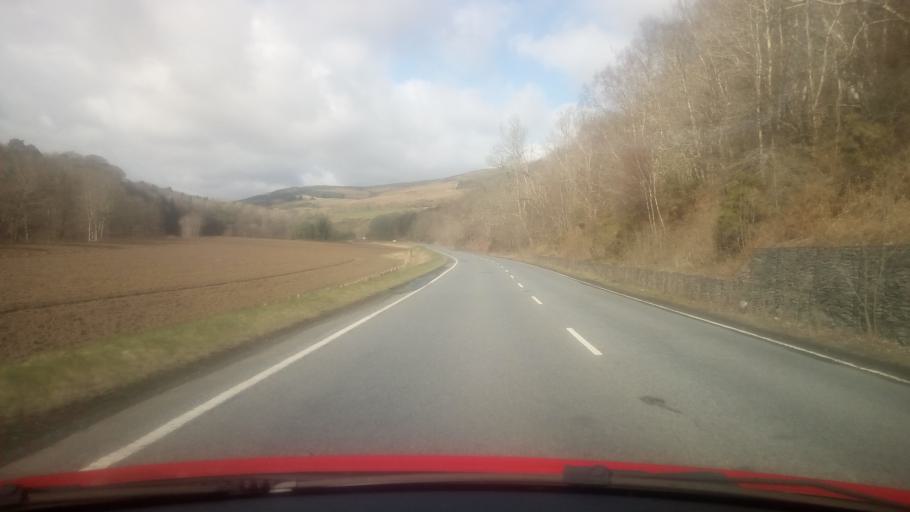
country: GB
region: Scotland
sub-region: The Scottish Borders
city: Selkirk
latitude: 55.6132
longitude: -2.9123
